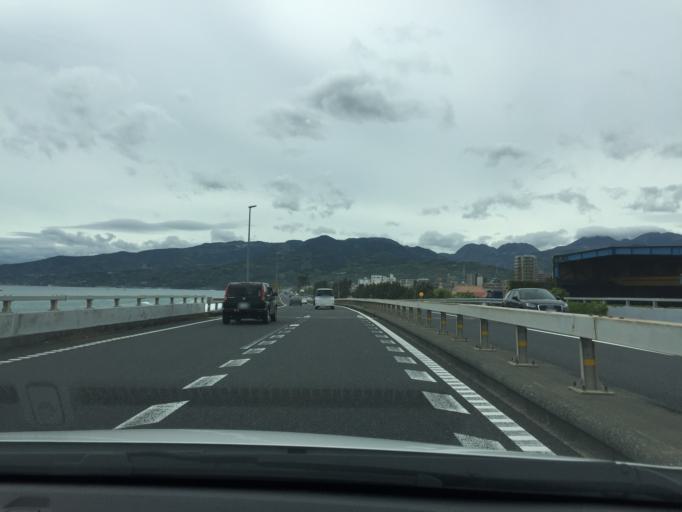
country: JP
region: Kanagawa
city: Odawara
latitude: 35.2546
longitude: 139.1712
